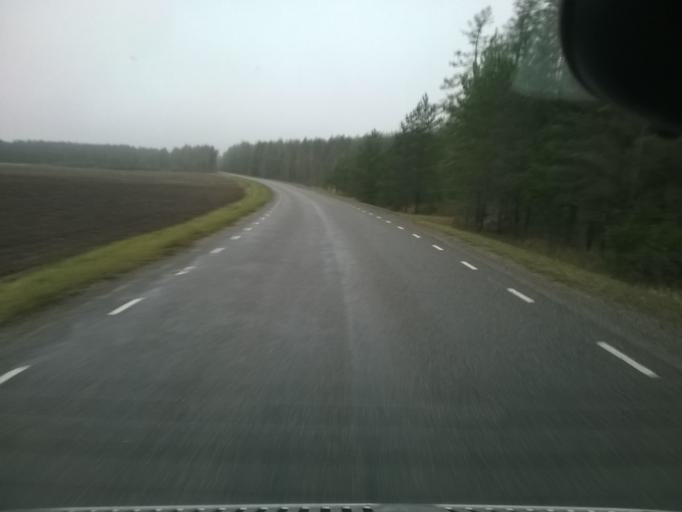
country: EE
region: Raplamaa
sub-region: Kohila vald
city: Kohila
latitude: 59.1846
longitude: 24.6600
